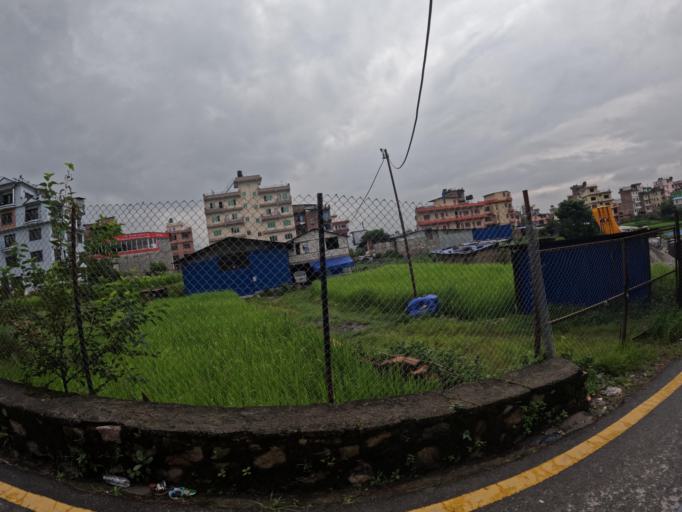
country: NP
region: Central Region
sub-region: Bagmati Zone
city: Kathmandu
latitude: 27.7639
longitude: 85.3297
